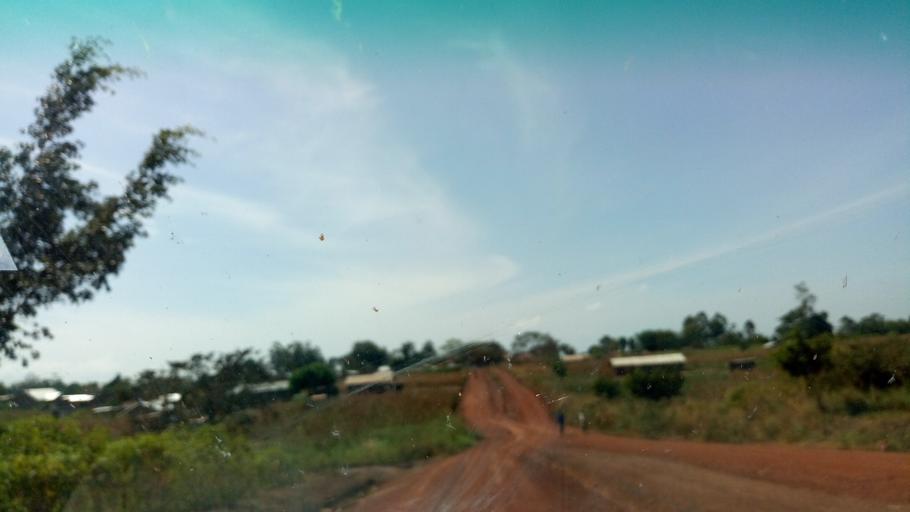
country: UG
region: Western Region
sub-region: Kiryandongo District
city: Kiryandongo
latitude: 1.9473
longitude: 32.1579
